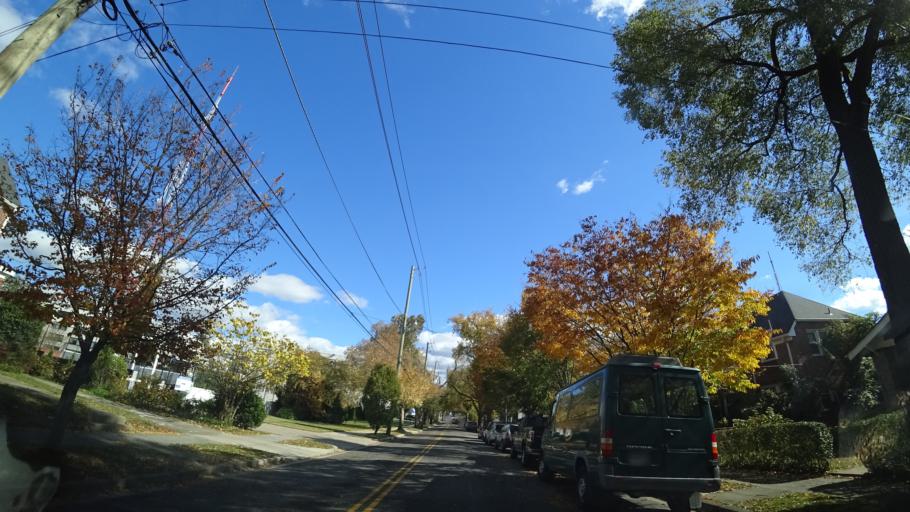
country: US
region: Maryland
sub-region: Montgomery County
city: Friendship Village
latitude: 38.9547
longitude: -77.0845
